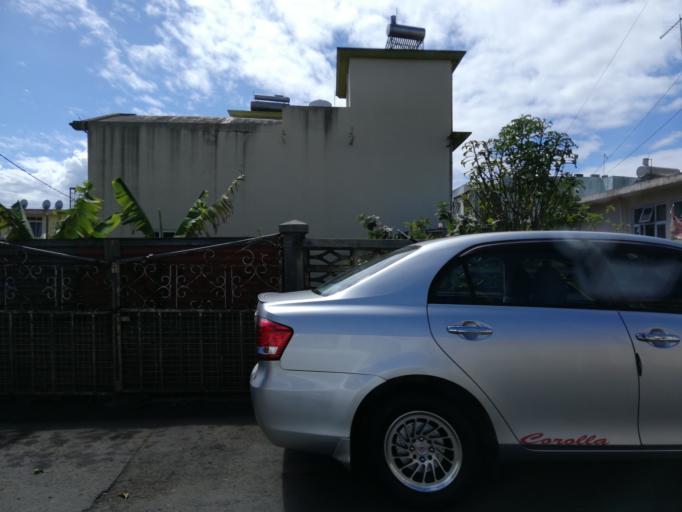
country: MU
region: Plaines Wilhems
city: Ebene
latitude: -20.2329
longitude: 57.4669
